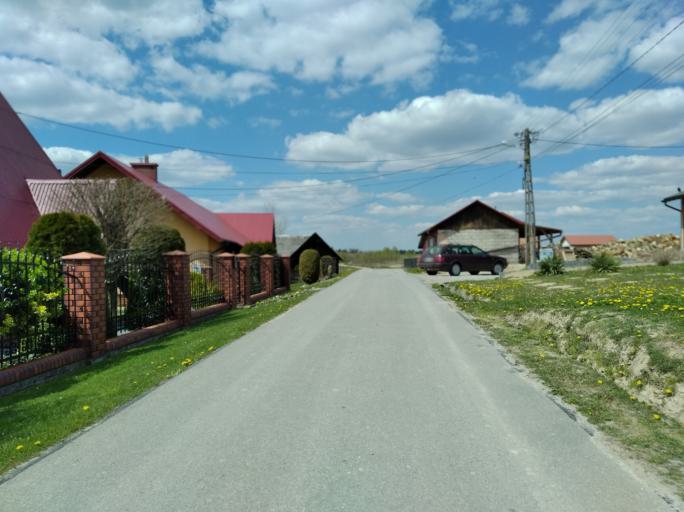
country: PL
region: Subcarpathian Voivodeship
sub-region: Powiat brzozowski
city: Jablonka
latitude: 49.7389
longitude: 22.0910
